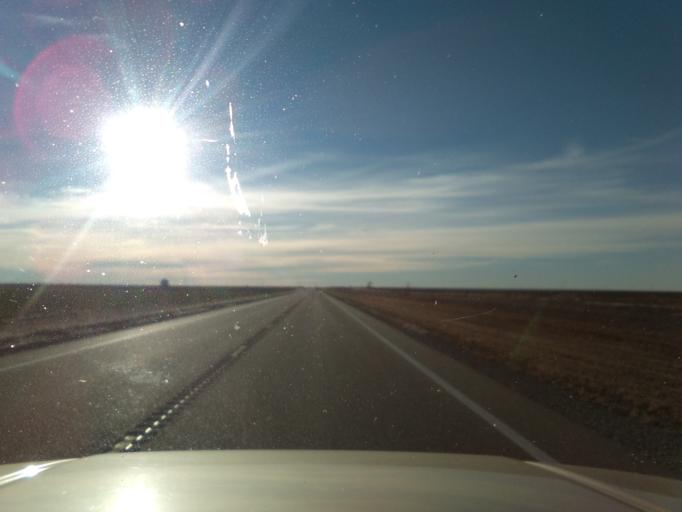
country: US
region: Kansas
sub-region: Sheridan County
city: Hoxie
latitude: 39.5001
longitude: -100.6693
